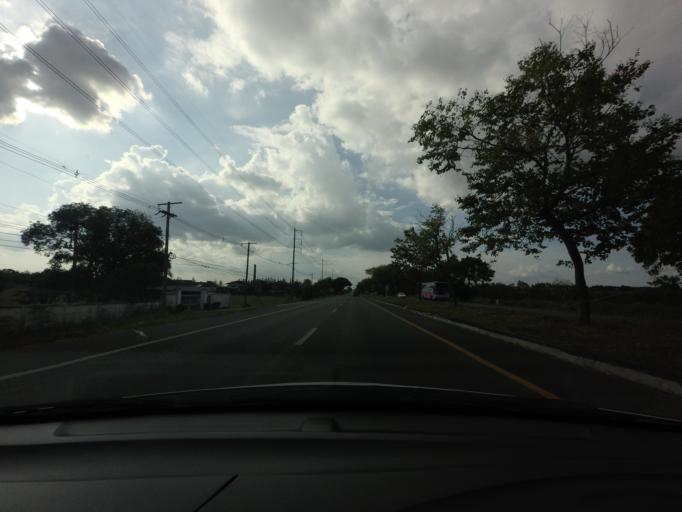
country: TH
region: Nakhon Nayok
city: Nakhon Nayok
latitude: 14.2192
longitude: 101.1566
